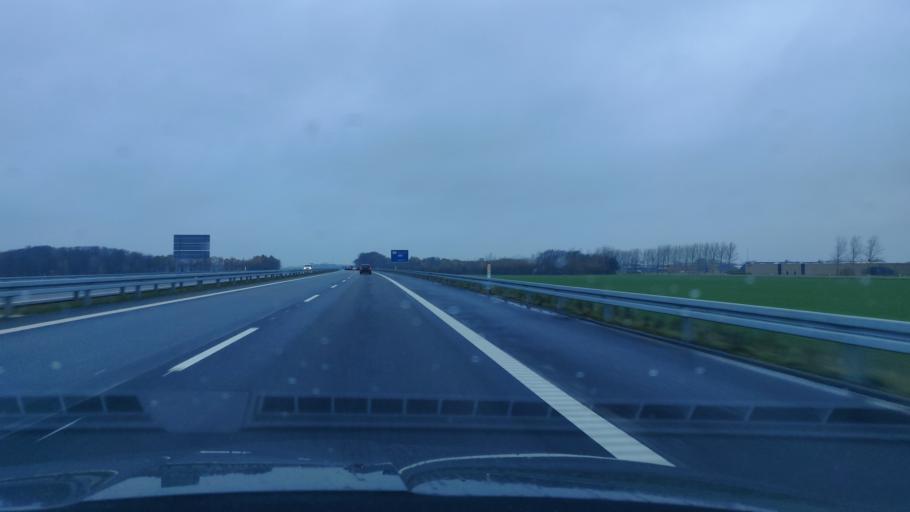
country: DK
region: Central Jutland
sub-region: Herning Kommune
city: Avlum
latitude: 56.2491
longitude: 8.7932
